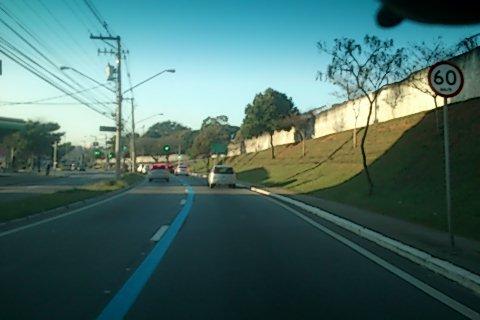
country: BR
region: Sao Paulo
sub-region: Sao Jose Dos Campos
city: Sao Jose dos Campos
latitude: -23.2000
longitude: -45.8640
